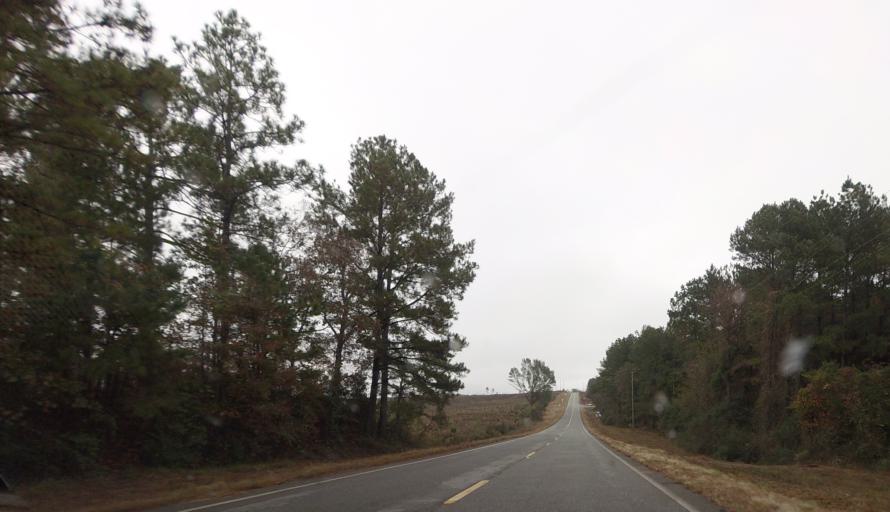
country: US
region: Georgia
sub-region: Taylor County
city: Butler
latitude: 32.4436
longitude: -84.3685
